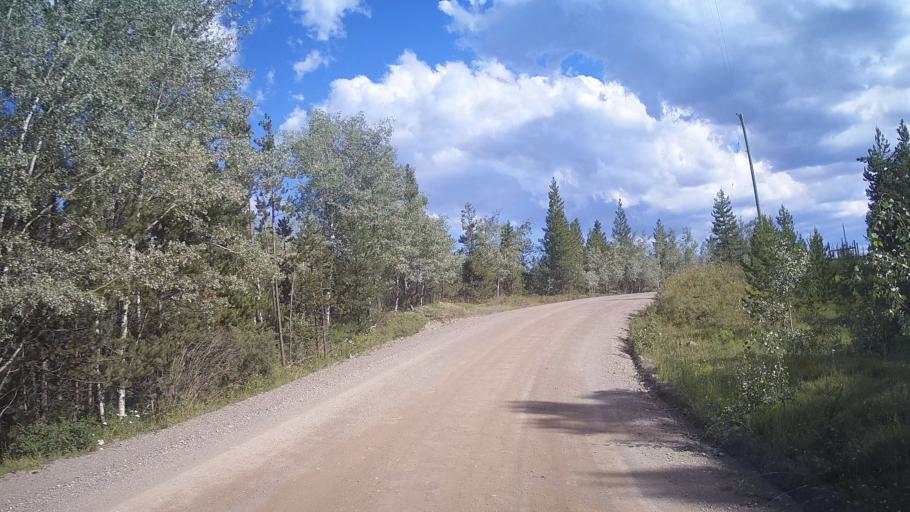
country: CA
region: British Columbia
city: Cache Creek
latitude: 51.2750
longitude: -121.7285
